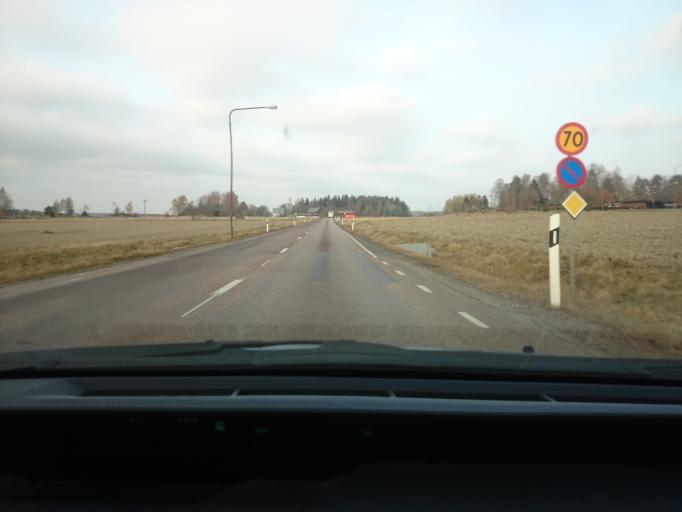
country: SE
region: Vaestmanland
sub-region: Vasteras
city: Vasteras
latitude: 59.6469
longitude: 16.4997
